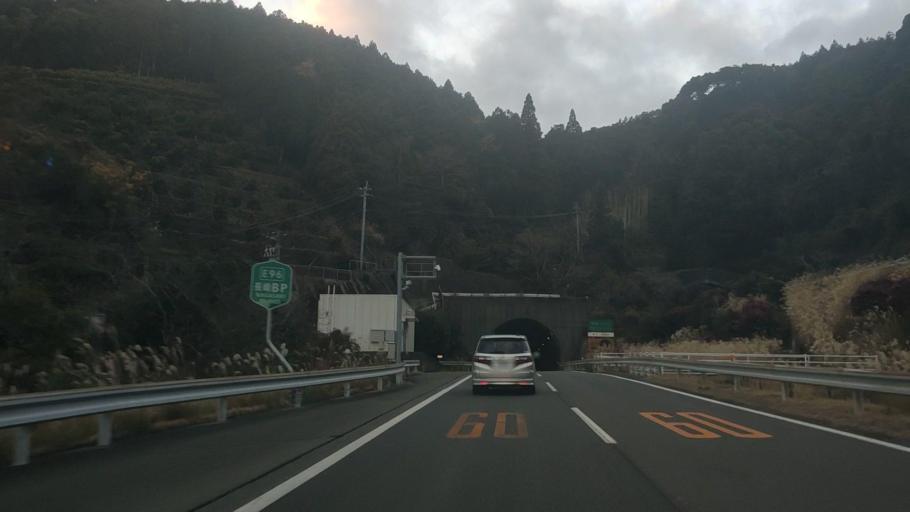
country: JP
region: Nagasaki
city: Obita
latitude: 32.8125
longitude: 129.9314
